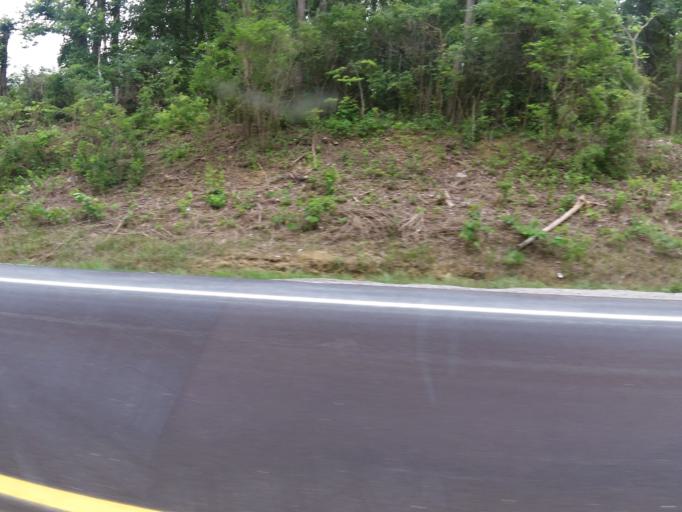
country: US
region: Ohio
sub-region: Clinton County
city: Blanchester
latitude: 39.2451
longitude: -83.9050
